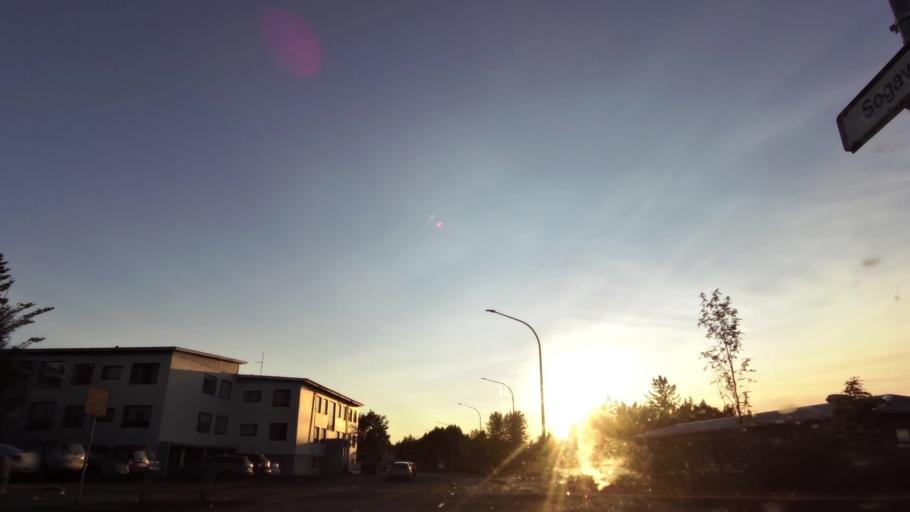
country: IS
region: Capital Region
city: Reykjavik
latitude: 64.1276
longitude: -21.8689
